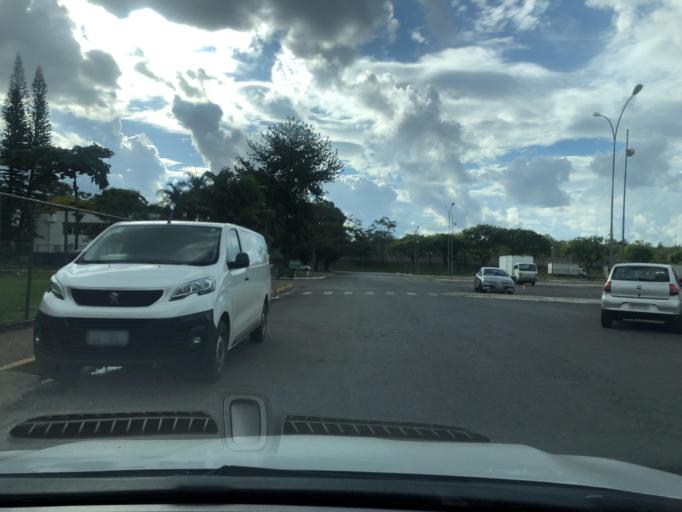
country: BR
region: Federal District
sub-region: Brasilia
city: Brasilia
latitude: -15.7932
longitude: -47.9495
